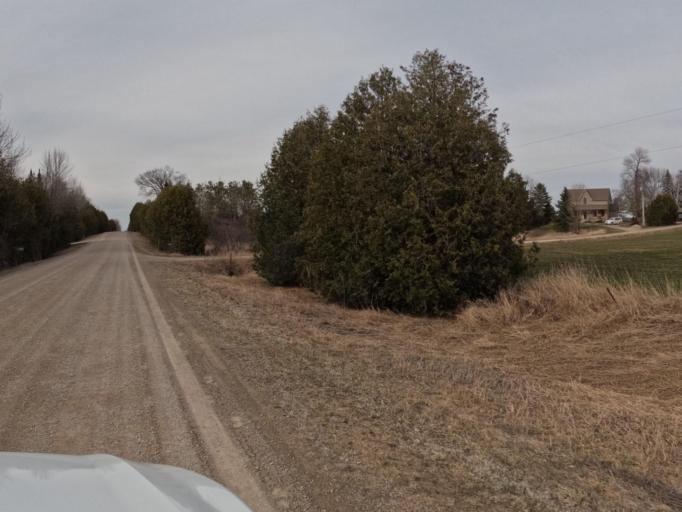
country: CA
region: Ontario
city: Orangeville
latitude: 43.9277
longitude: -80.2571
